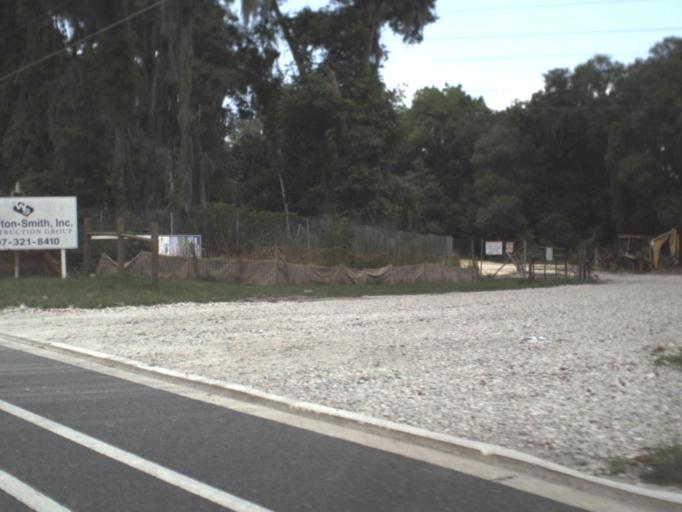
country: US
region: Florida
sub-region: Alachua County
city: Gainesville
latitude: 29.6197
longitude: -82.3299
